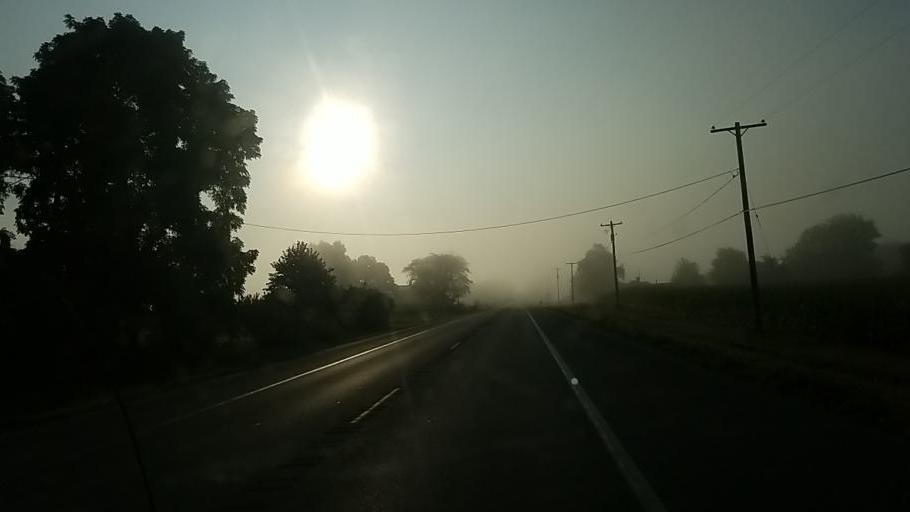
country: US
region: Michigan
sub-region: Newaygo County
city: Fremont
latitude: 43.4673
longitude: -86.0162
